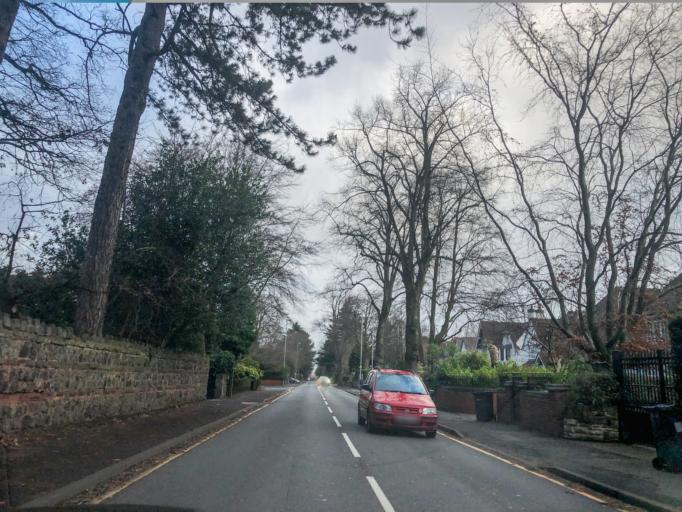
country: GB
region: England
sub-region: City and Borough of Birmingham
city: Birmingham
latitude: 52.4450
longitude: -1.9015
